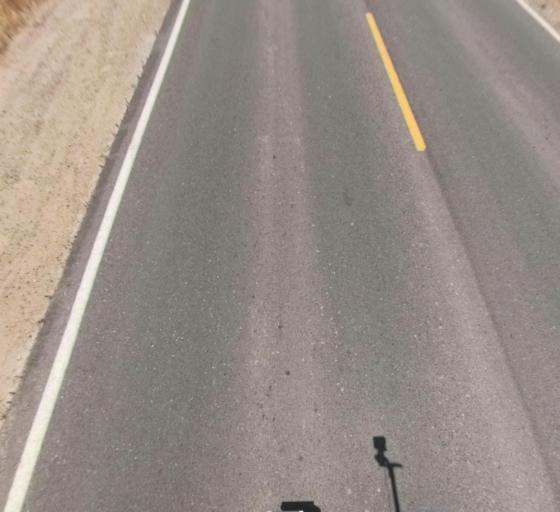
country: US
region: California
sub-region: Madera County
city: Bonadelle Ranchos-Madera Ranchos
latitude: 36.9683
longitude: -119.8938
